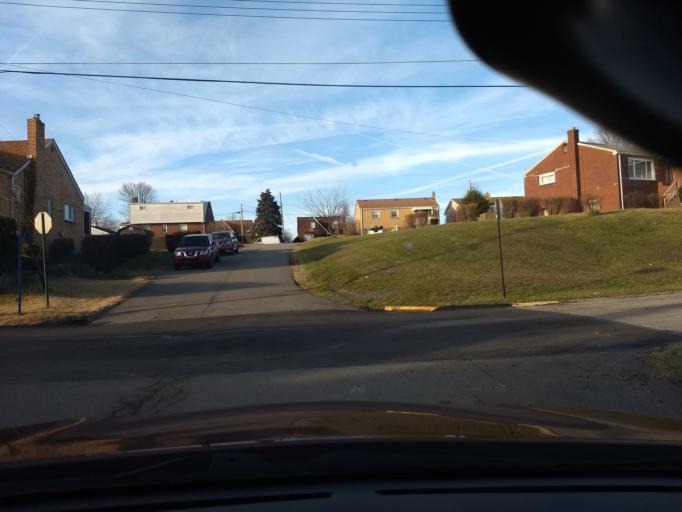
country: US
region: Pennsylvania
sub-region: Allegheny County
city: Whitaker
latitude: 40.4017
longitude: -79.8856
